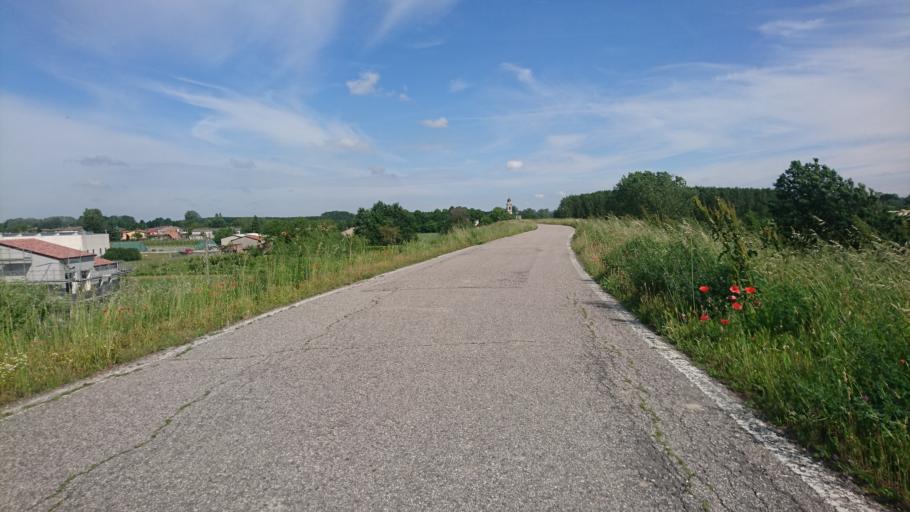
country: IT
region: Lombardy
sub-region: Provincia di Mantova
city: Borgofranco sul Po
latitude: 45.0470
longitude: 11.2112
